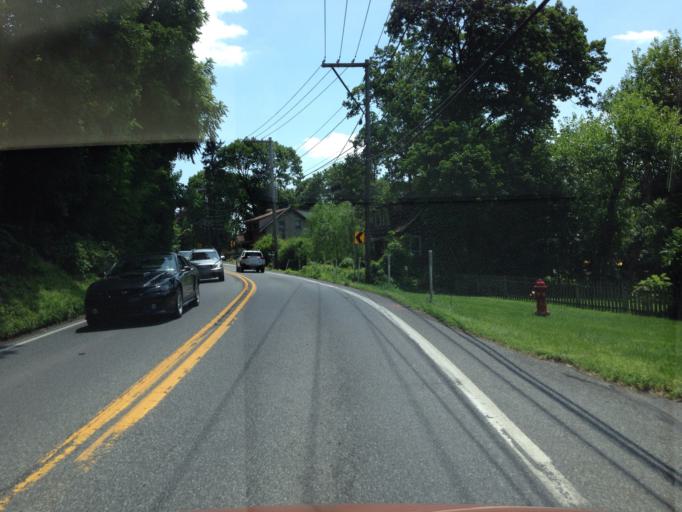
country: US
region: Pennsylvania
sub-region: Lancaster County
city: East Petersburg
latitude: 40.0912
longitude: -76.3302
